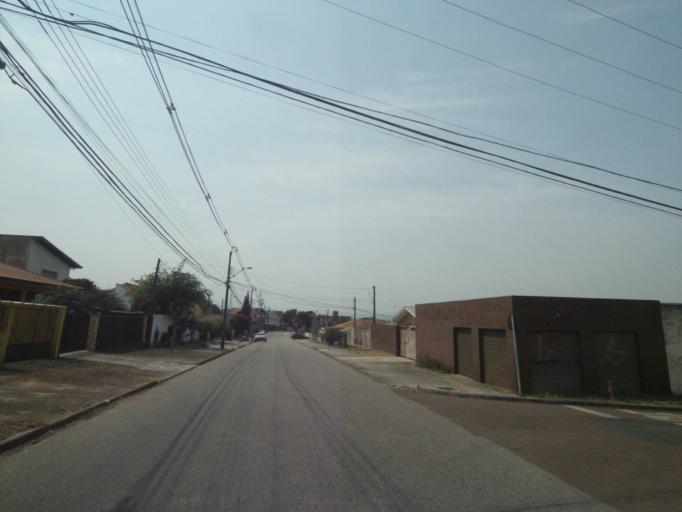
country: BR
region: Parana
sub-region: Pinhais
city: Pinhais
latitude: -25.4853
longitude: -49.2107
